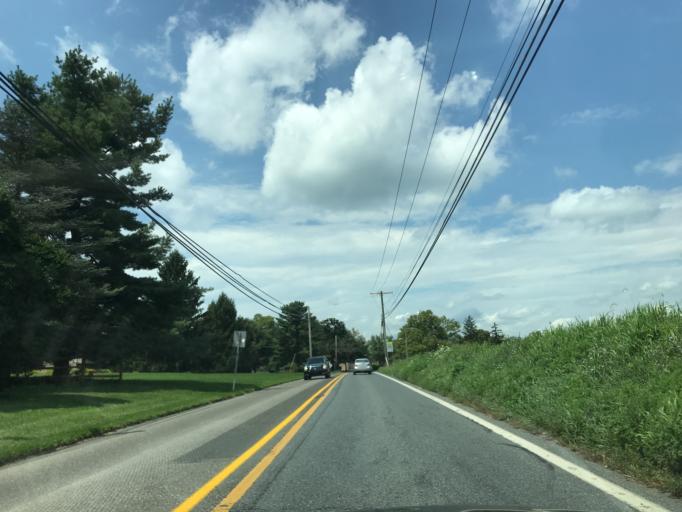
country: US
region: Pennsylvania
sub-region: York County
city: New Freedom
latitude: 39.6656
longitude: -76.7095
